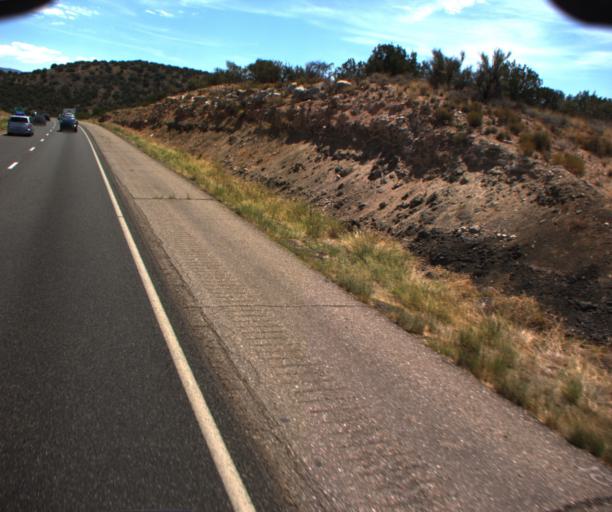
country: US
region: Arizona
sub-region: Yavapai County
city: Lake Montezuma
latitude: 34.6759
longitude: -111.7610
